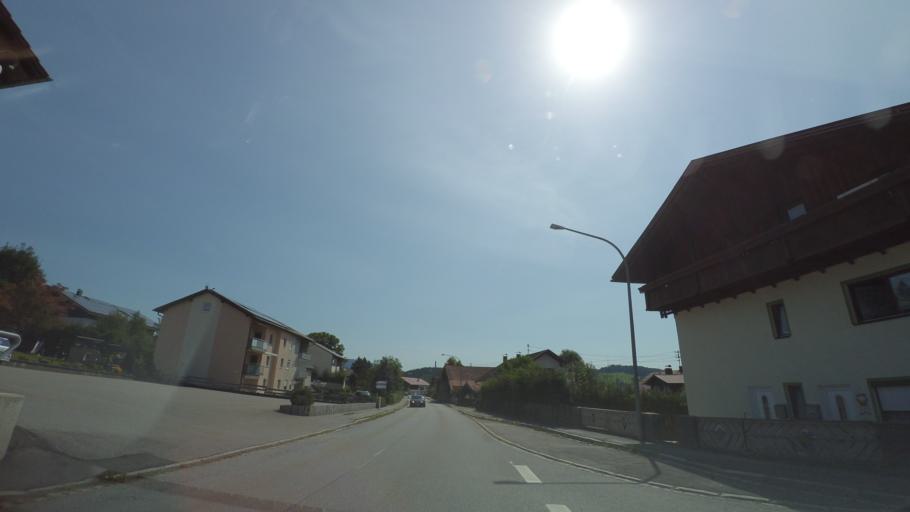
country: DE
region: Bavaria
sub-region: Lower Bavaria
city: Teisnach
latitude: 49.0443
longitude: 12.9841
